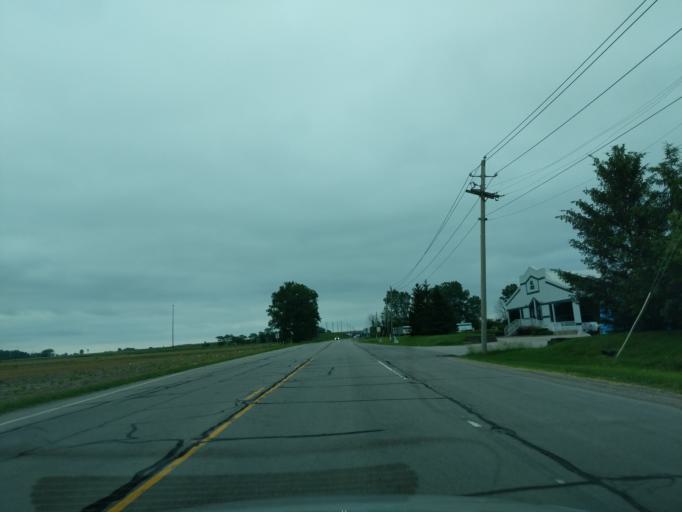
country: US
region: Indiana
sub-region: Madison County
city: Alexandria
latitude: 40.2770
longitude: -85.5641
